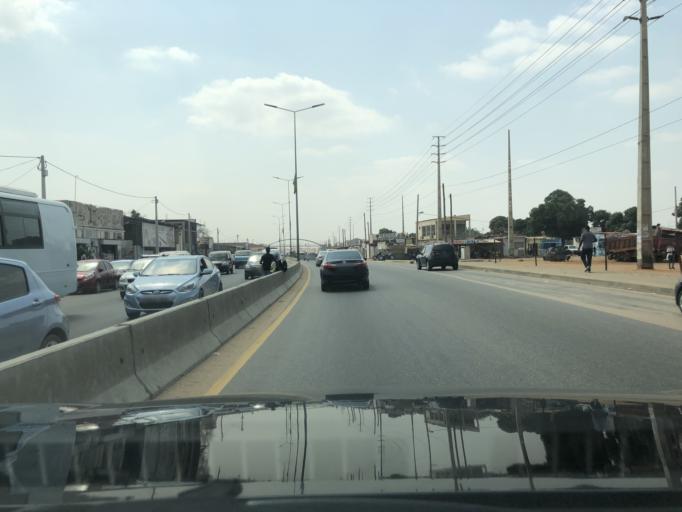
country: AO
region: Luanda
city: Luanda
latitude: -8.9361
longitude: 13.2628
